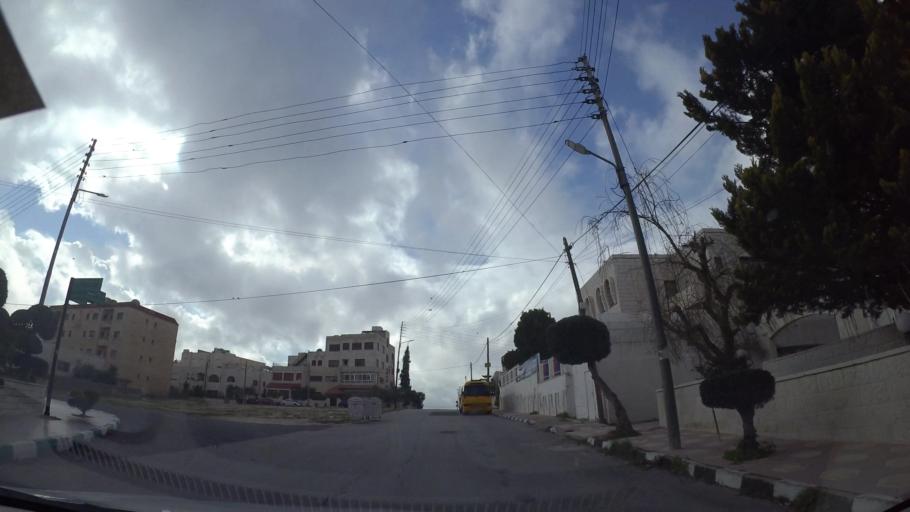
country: JO
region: Amman
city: Al Jubayhah
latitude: 32.0422
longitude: 35.8704
